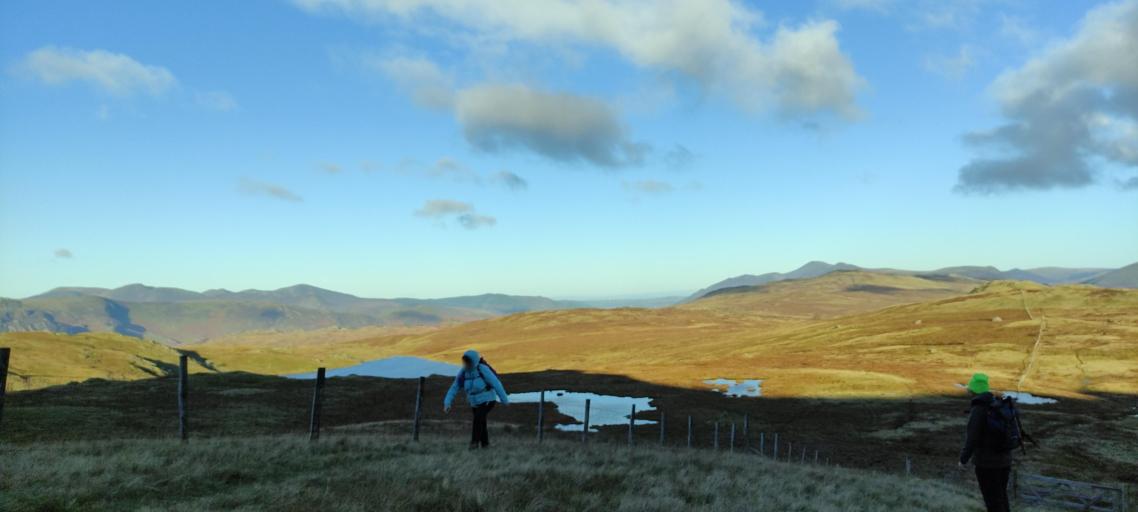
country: GB
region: England
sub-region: Cumbria
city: Keswick
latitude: 54.5123
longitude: -3.0881
